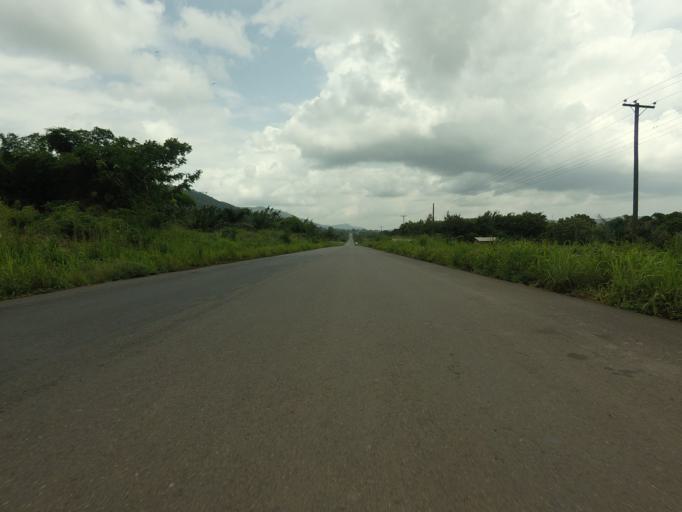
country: GH
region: Volta
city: Ho
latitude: 6.6190
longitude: 0.3059
